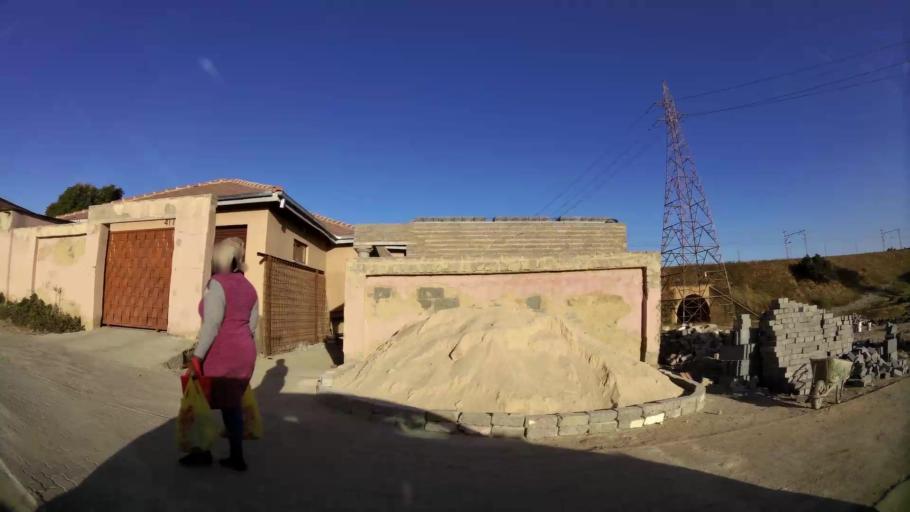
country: ZA
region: Gauteng
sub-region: Ekurhuleni Metropolitan Municipality
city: Tembisa
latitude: -26.0220
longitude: 28.2047
